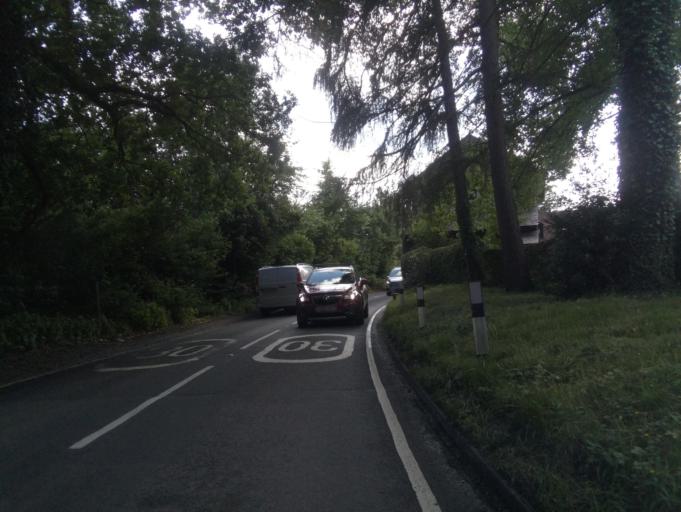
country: GB
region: England
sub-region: Hertfordshire
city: Chorleywood
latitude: 51.6679
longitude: -0.4641
